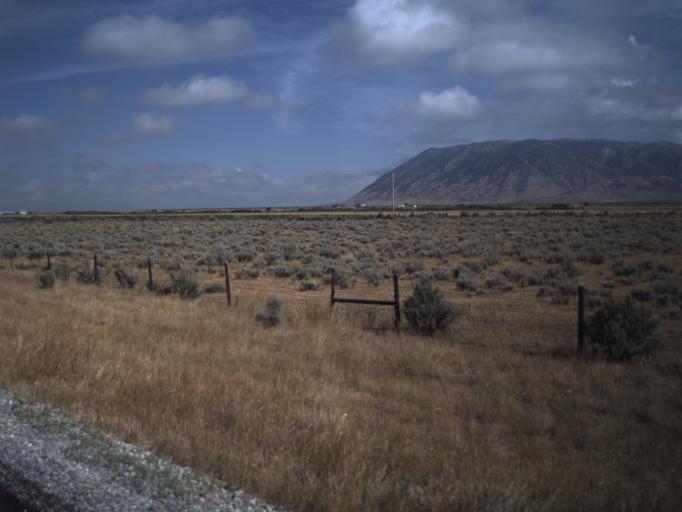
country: US
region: Utah
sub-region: Rich County
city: Randolph
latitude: 41.5747
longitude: -111.1629
